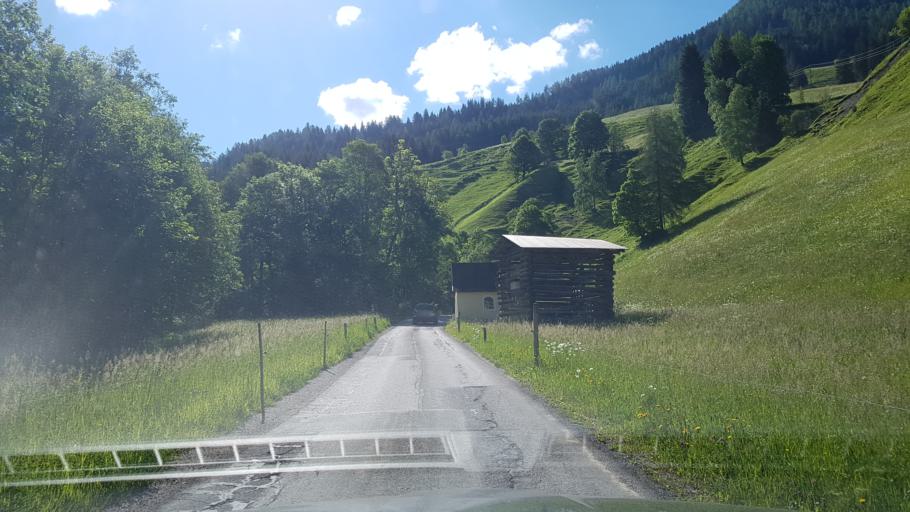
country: AT
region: Salzburg
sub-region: Politischer Bezirk Sankt Johann im Pongau
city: Huttschlag
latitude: 47.2350
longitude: 13.2513
